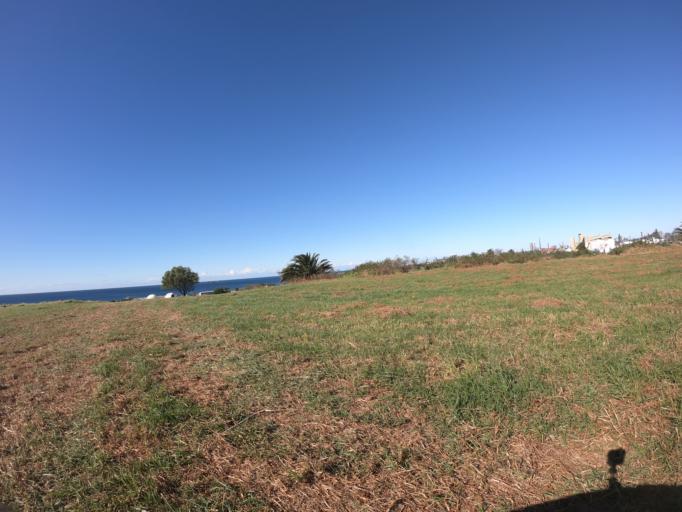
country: AU
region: New South Wales
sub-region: Wollongong
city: Coniston
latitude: -34.4416
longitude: 150.8944
